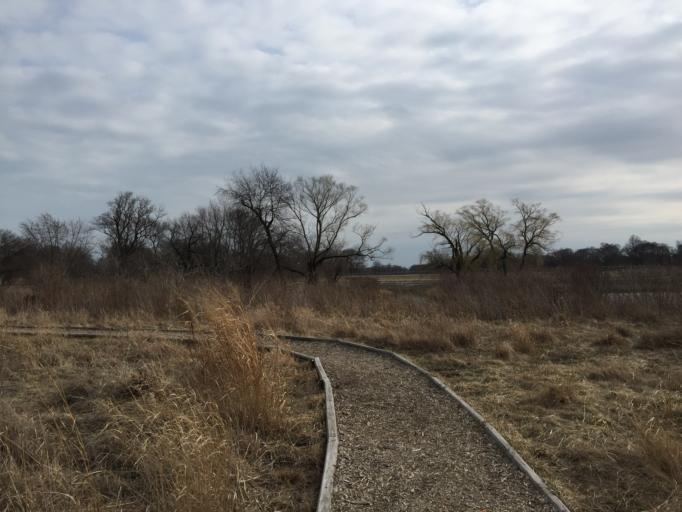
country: US
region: Illinois
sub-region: Cook County
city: Chicago
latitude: 41.7842
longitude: -87.5799
